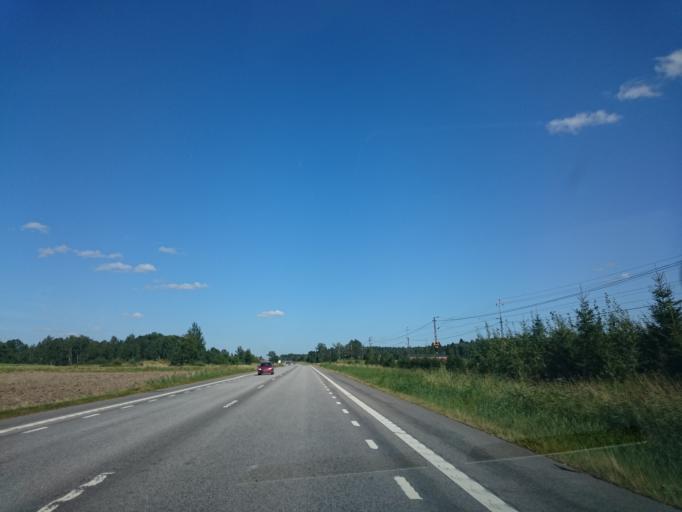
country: SE
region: OEstergoetland
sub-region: Linkopings Kommun
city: Linghem
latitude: 58.4524
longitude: 15.8390
